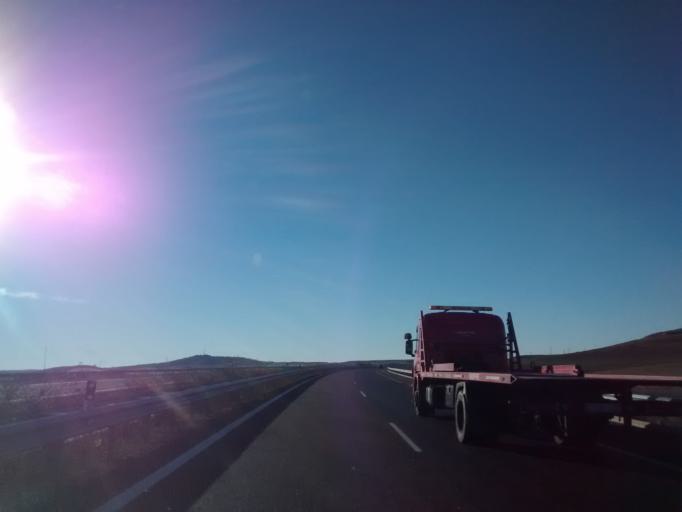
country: ES
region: Castille and Leon
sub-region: Provincia de Palencia
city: Herrera de Pisuerga
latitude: 42.5767
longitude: -4.3455
